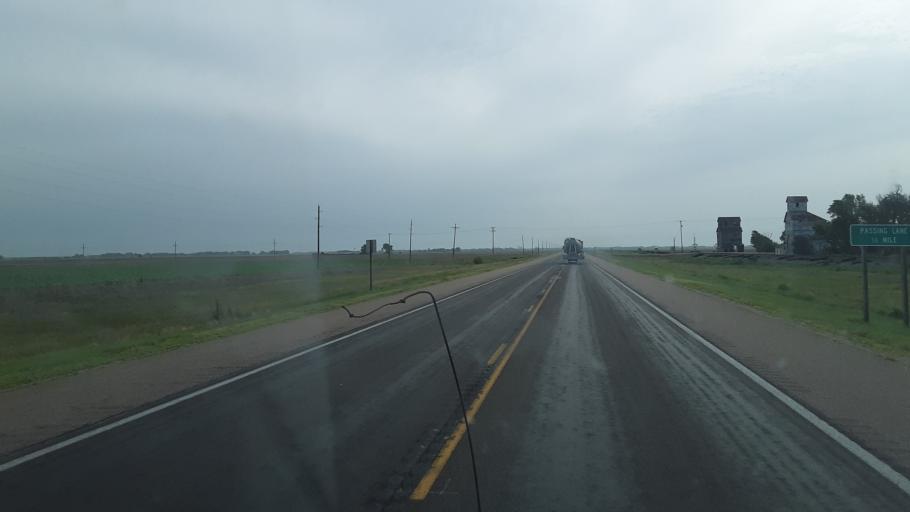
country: US
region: Kansas
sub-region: Edwards County
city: Kinsley
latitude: 37.9017
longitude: -99.4985
